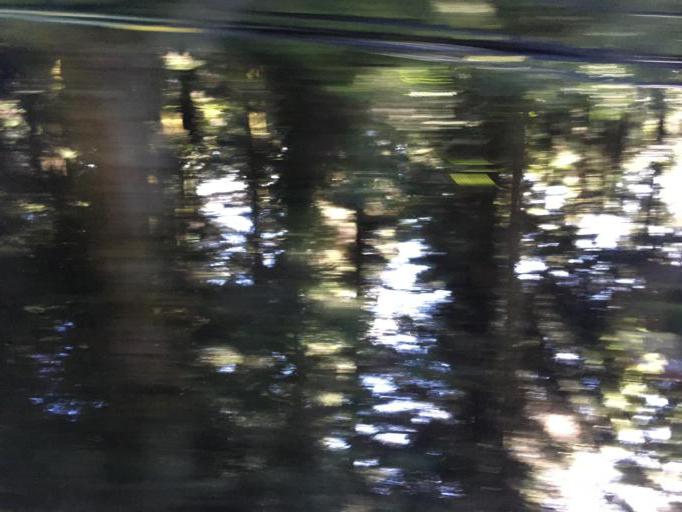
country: TW
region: Taiwan
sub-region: Yilan
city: Yilan
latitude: 24.4983
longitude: 121.5532
